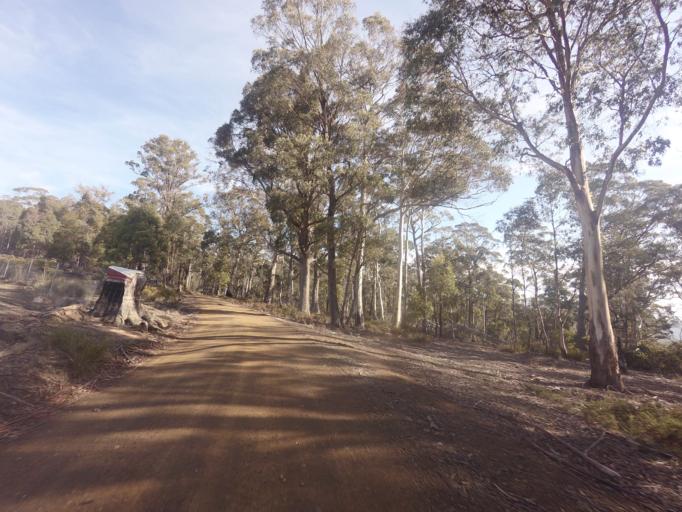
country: AU
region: Tasmania
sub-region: Sorell
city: Sorell
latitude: -42.5228
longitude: 147.4729
